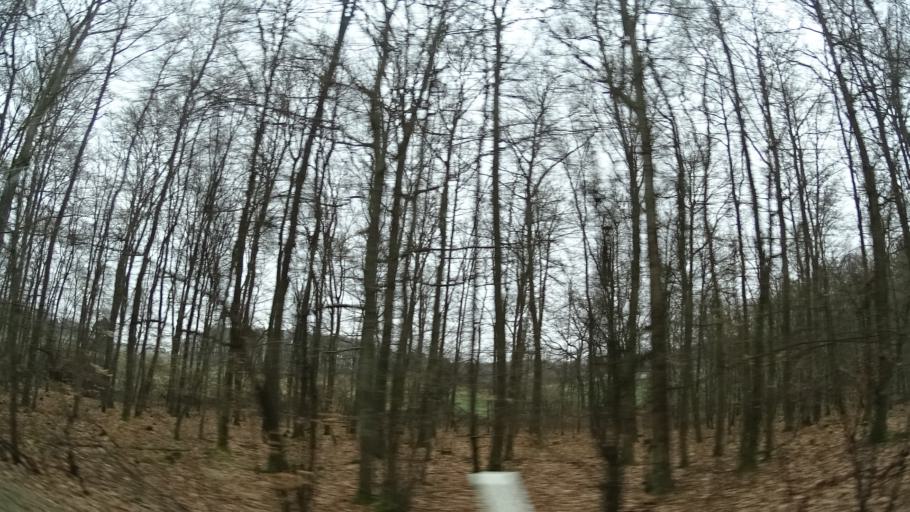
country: DE
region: Rheinland-Pfalz
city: Oberwiesen
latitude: 49.6664
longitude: 7.9759
